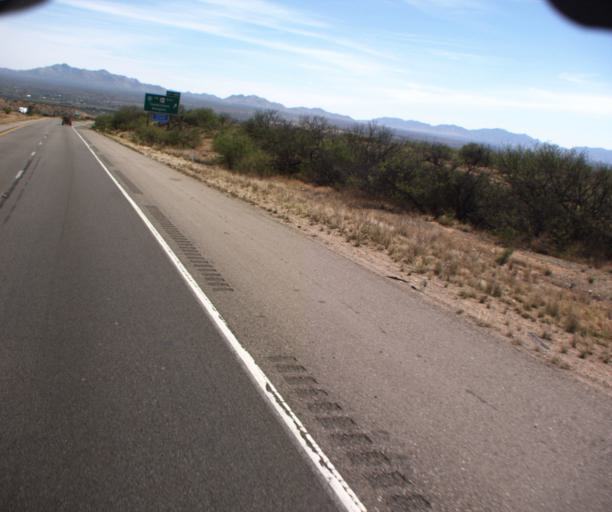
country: US
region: Arizona
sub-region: Cochise County
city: Whetstone
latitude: 31.9686
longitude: -110.3320
